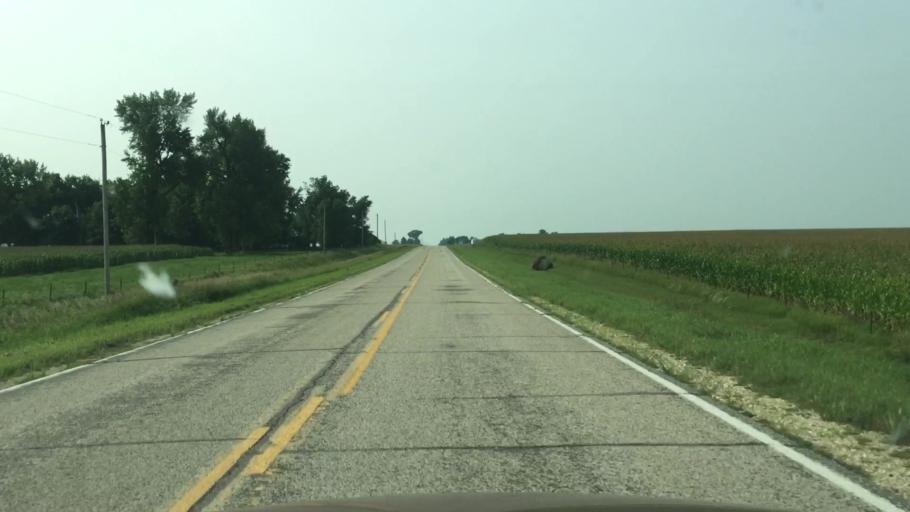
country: US
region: Iowa
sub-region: O'Brien County
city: Sheldon
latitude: 43.2792
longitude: -95.7829
